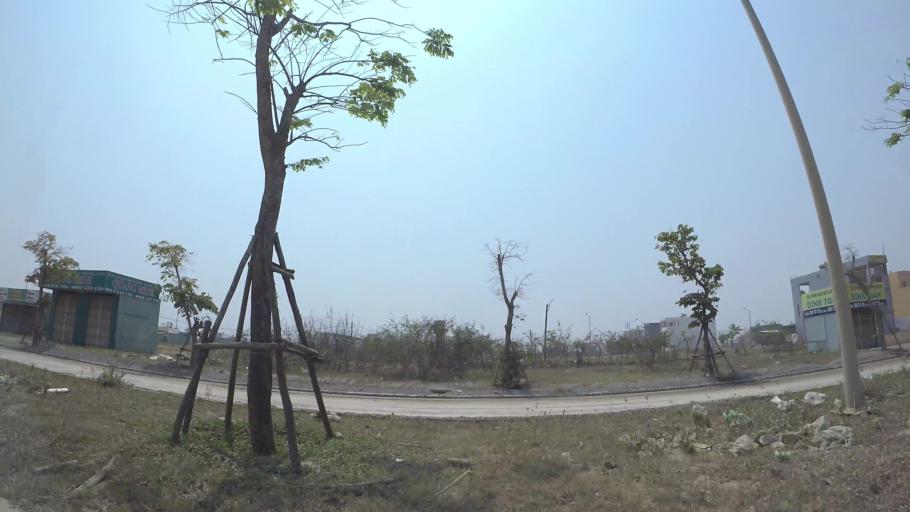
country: VN
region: Da Nang
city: Ngu Hanh Son
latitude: 16.0100
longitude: 108.2420
